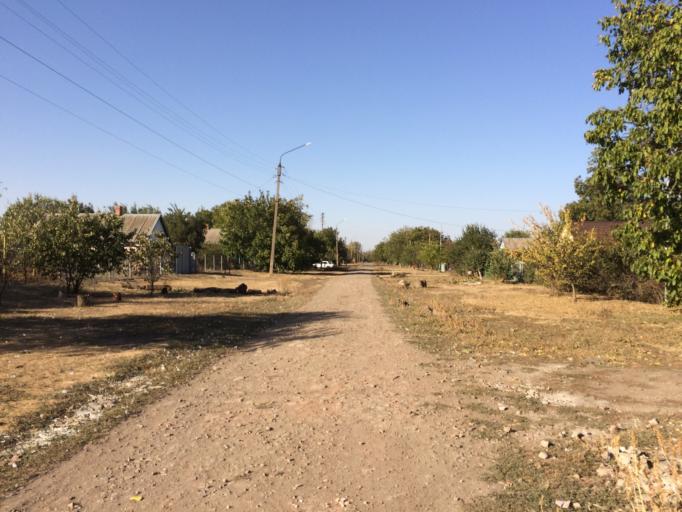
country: RU
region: Rostov
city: Gigant
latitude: 46.5198
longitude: 41.1882
